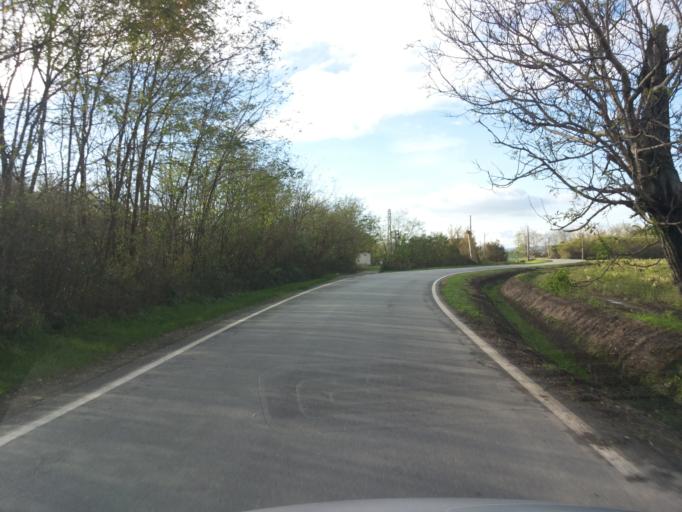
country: IT
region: Piedmont
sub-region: Provincia di Vercelli
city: Santhia
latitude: 45.3600
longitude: 8.1432
